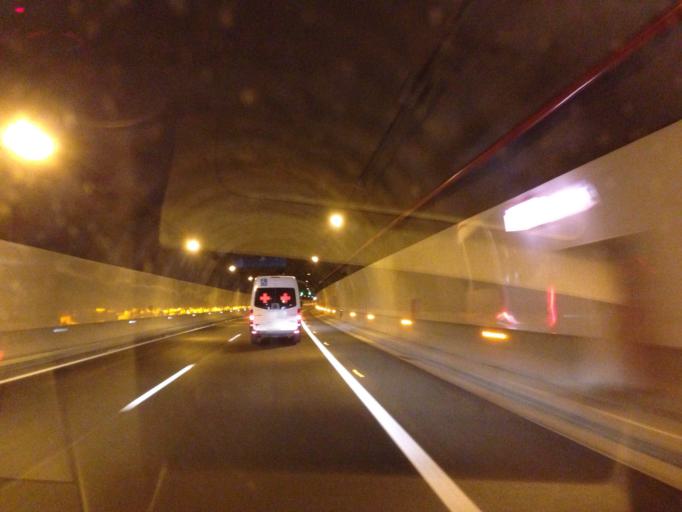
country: ES
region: Canary Islands
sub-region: Provincia de Las Palmas
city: Puerto Rico
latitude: 27.8104
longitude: -15.7276
